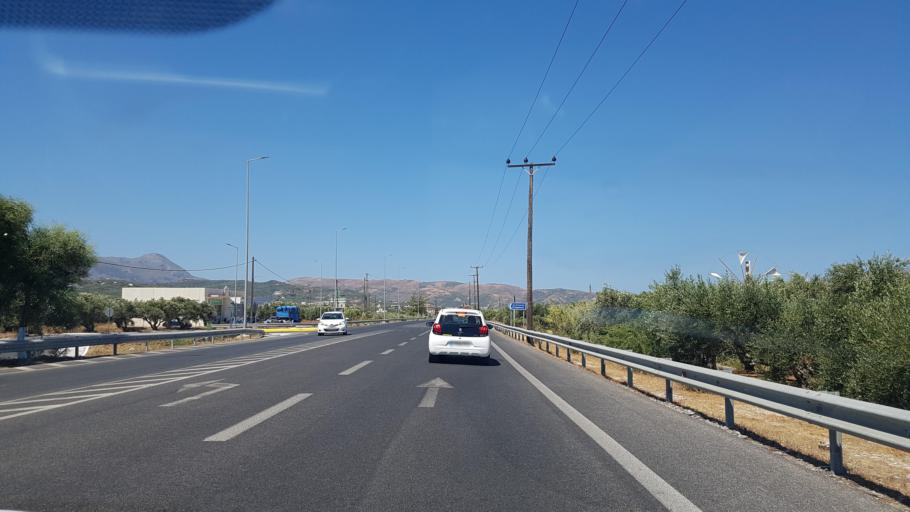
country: GR
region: Crete
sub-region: Nomos Chanias
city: Kissamos
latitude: 35.4975
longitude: 23.6987
